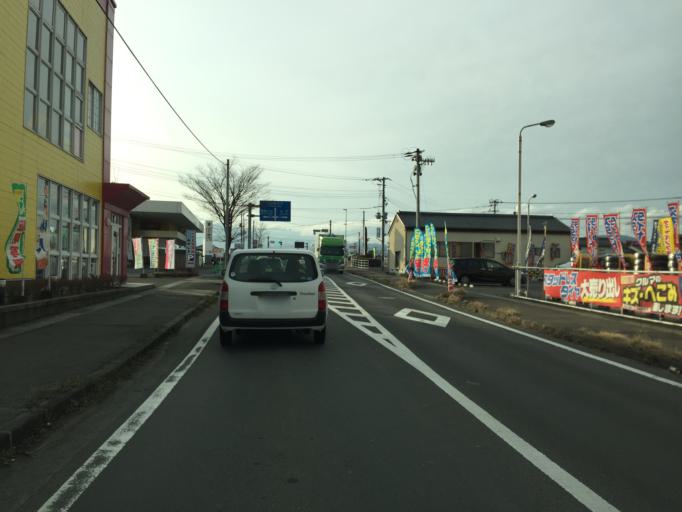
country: JP
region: Fukushima
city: Fukushima-shi
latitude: 37.7849
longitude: 140.4647
